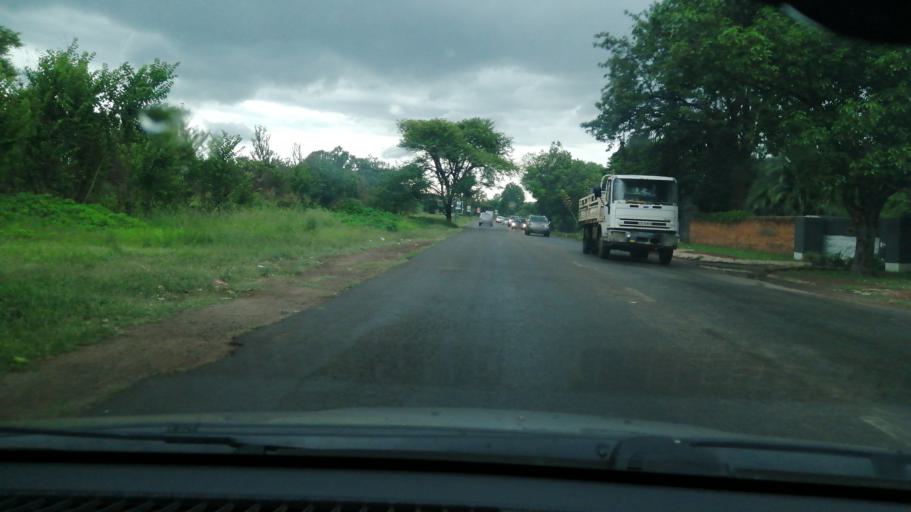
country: ZW
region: Harare
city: Harare
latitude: -17.7903
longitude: 31.0499
